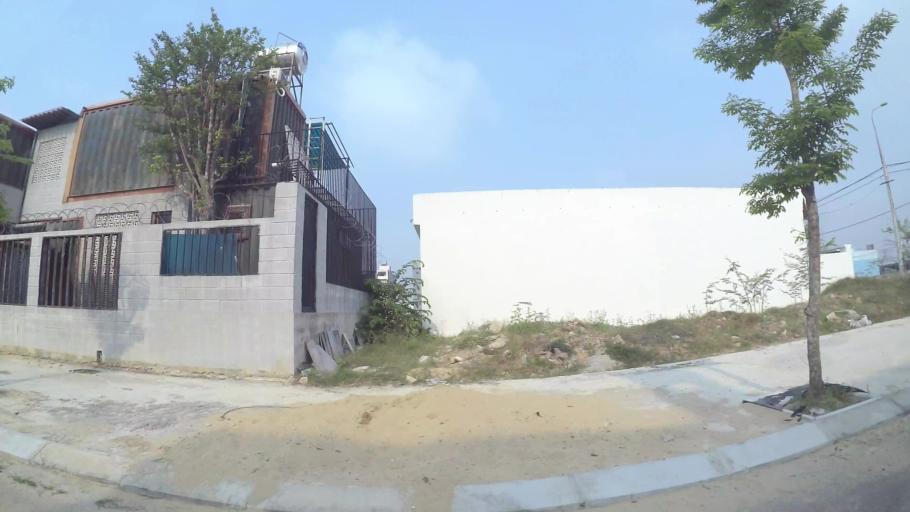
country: VN
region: Da Nang
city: Ngu Hanh Son
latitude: 16.0124
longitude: 108.2310
